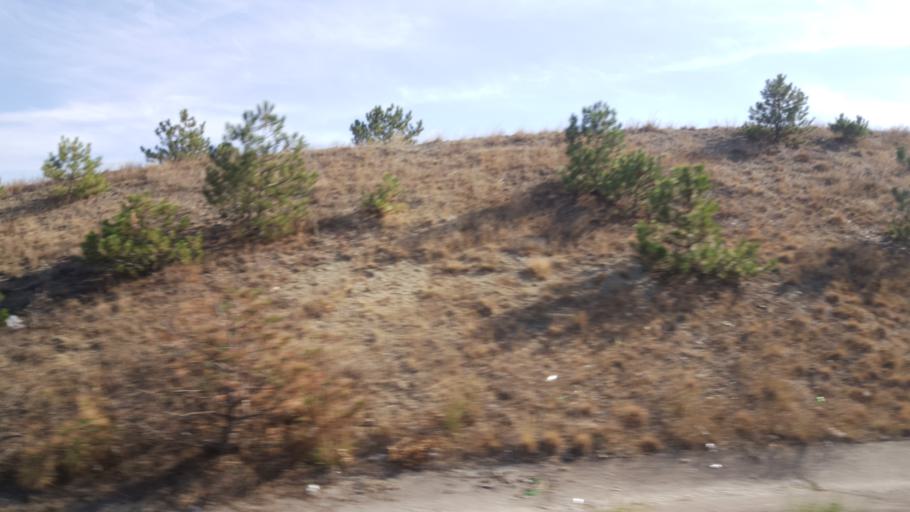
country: TR
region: Ankara
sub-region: Goelbasi
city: Golbasi
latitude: 39.8132
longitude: 32.7982
